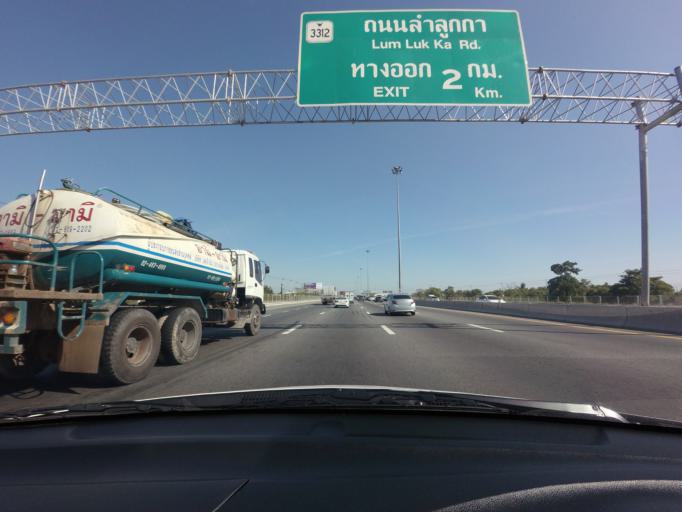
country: TH
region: Pathum Thani
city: Lam Luk Ka
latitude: 13.9094
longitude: 100.6993
